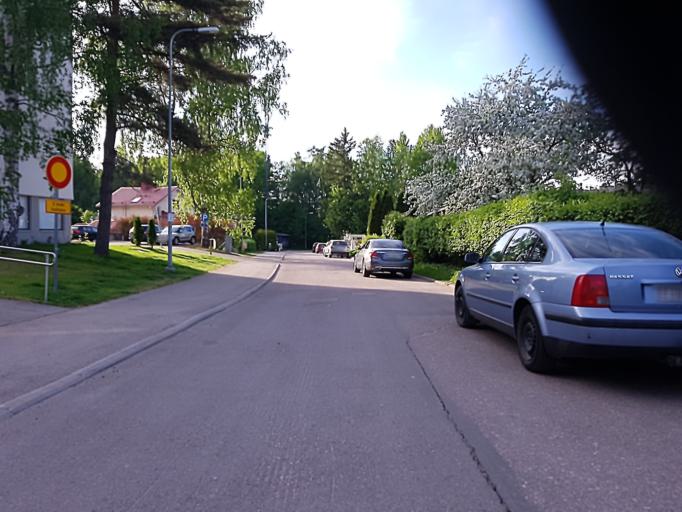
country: FI
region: Uusimaa
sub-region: Helsinki
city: Helsinki
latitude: 60.2500
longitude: 24.9237
